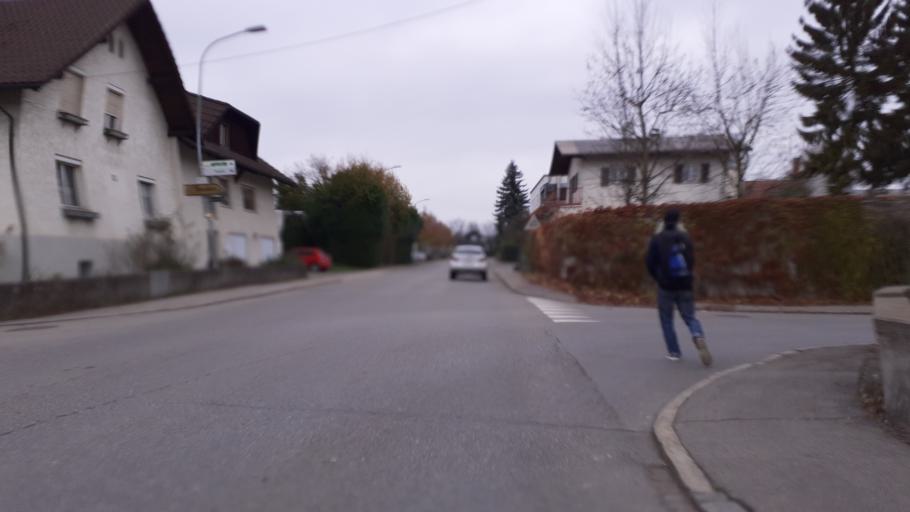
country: AT
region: Vorarlberg
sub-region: Politischer Bezirk Dornbirn
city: Lustenau
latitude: 47.4166
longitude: 9.6656
